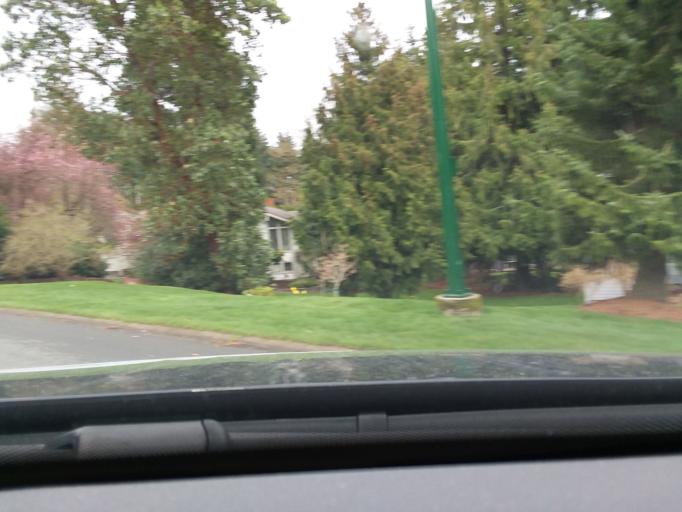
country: CA
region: British Columbia
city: North Saanich
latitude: 48.6144
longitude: -123.4228
